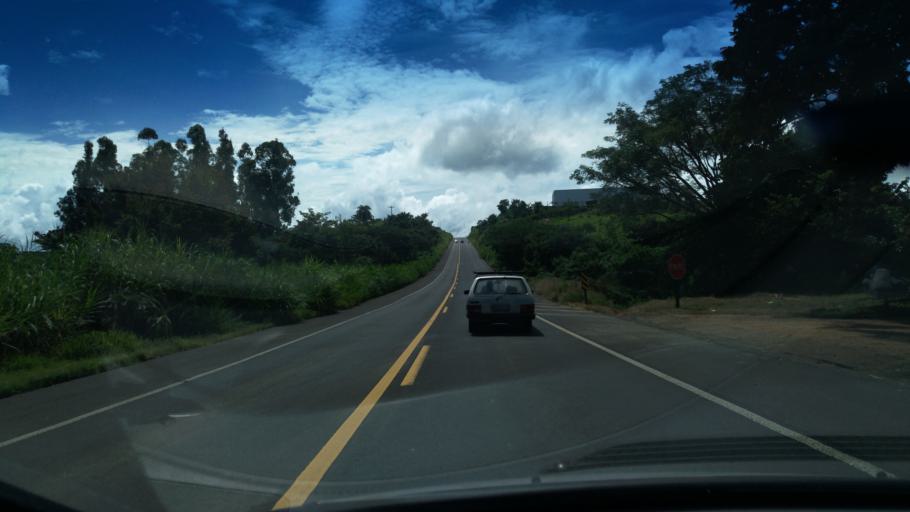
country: BR
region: Sao Paulo
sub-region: Santo Antonio Do Jardim
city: Espirito Santo do Pinhal
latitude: -22.1591
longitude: -46.7287
